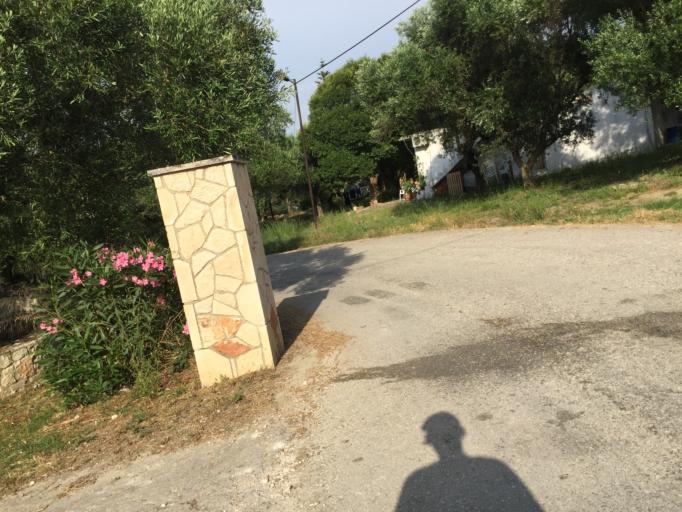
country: GR
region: Ionian Islands
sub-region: Nomos Zakynthou
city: Vanaton
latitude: 37.8121
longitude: 20.8600
